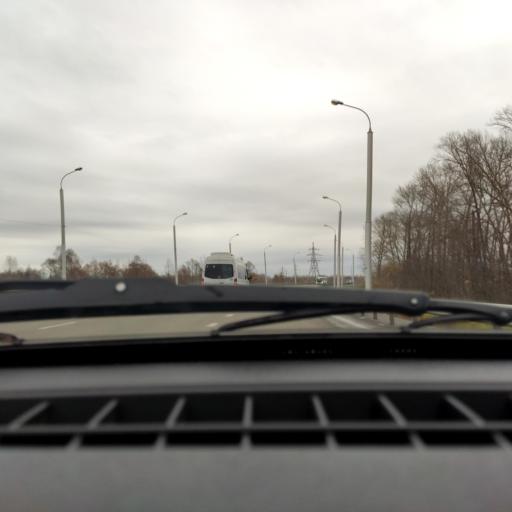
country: RU
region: Bashkortostan
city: Ufa
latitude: 54.8089
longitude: 56.1668
